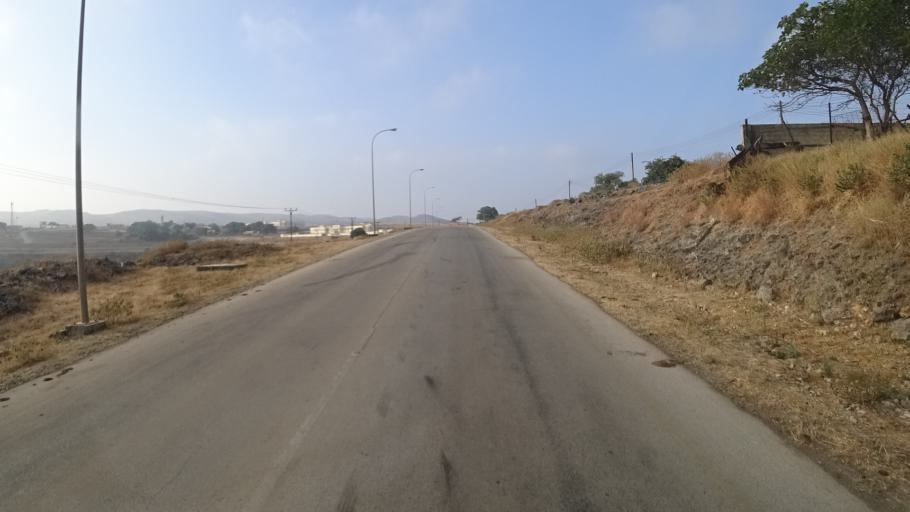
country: OM
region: Zufar
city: Salalah
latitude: 17.1226
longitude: 53.9997
